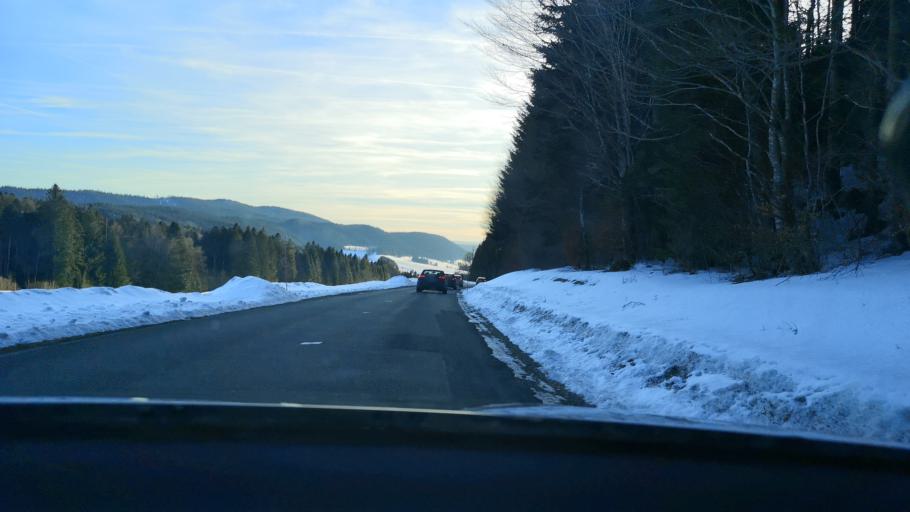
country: FR
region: Franche-Comte
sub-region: Departement du Doubs
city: Gilley
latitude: 46.9601
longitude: 6.4665
